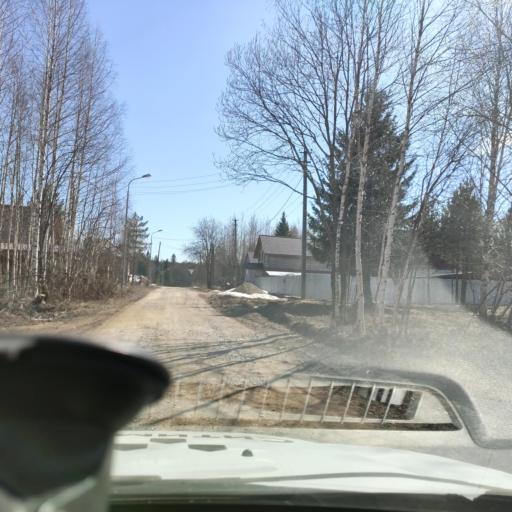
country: RU
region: Perm
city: Ferma
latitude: 57.9284
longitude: 56.4210
